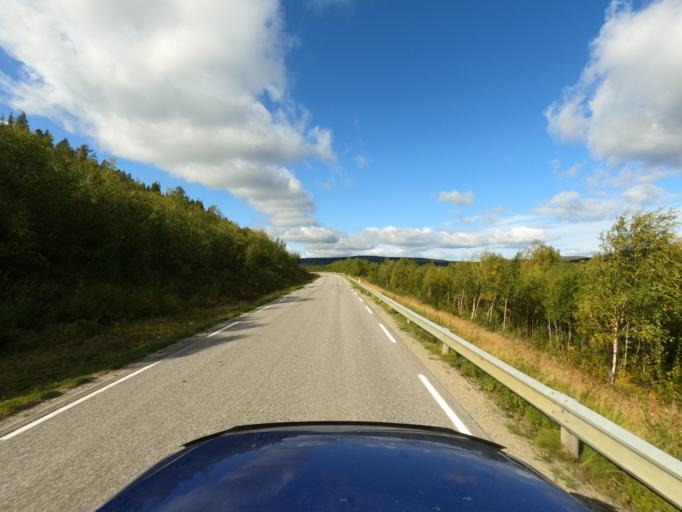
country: NO
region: Finnmark Fylke
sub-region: Karasjok
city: Karasjohka
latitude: 69.4564
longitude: 25.5629
